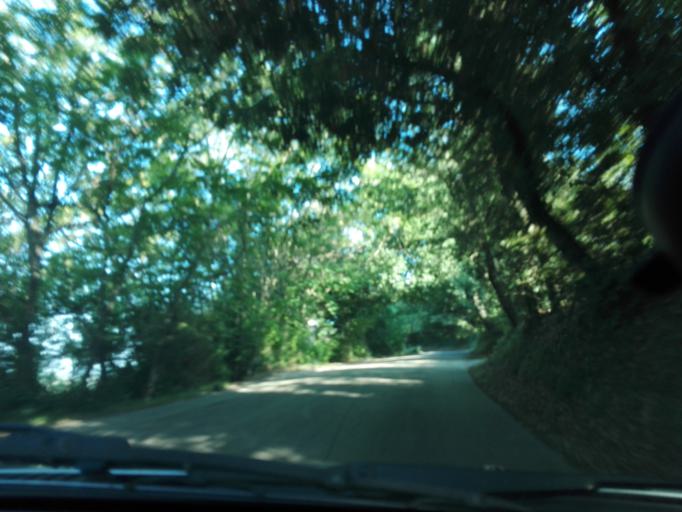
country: IT
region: Abruzzo
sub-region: Provincia di Pescara
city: Cappelle sul Tavo
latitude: 42.4479
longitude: 14.0911
